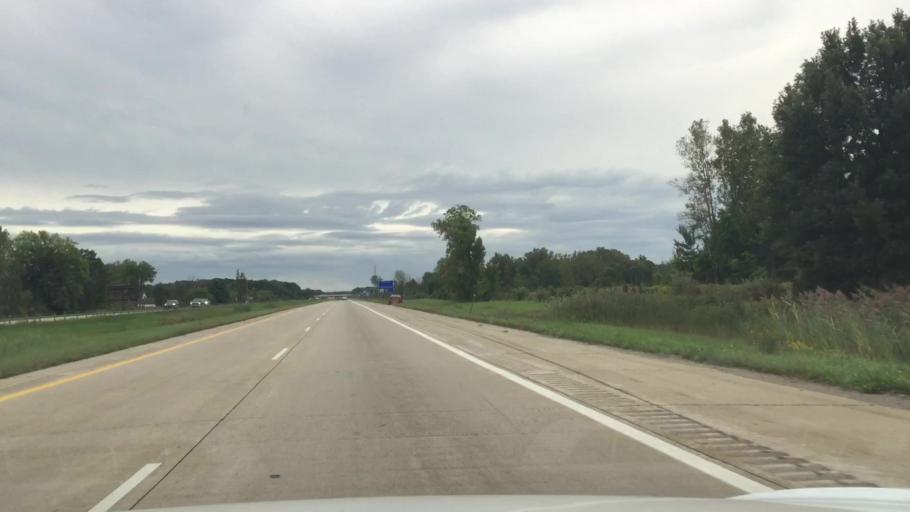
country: US
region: Michigan
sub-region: Saint Clair County
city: Marysville
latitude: 42.9349
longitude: -82.5070
